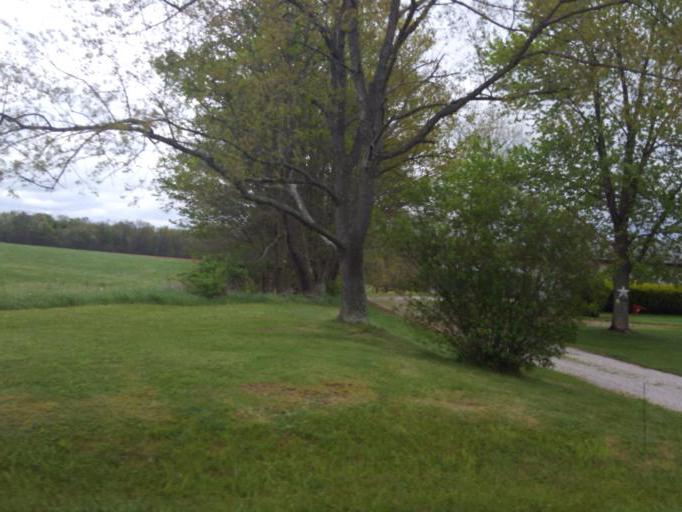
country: US
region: Ohio
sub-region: Knox County
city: Fredericktown
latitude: 40.5451
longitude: -82.5078
